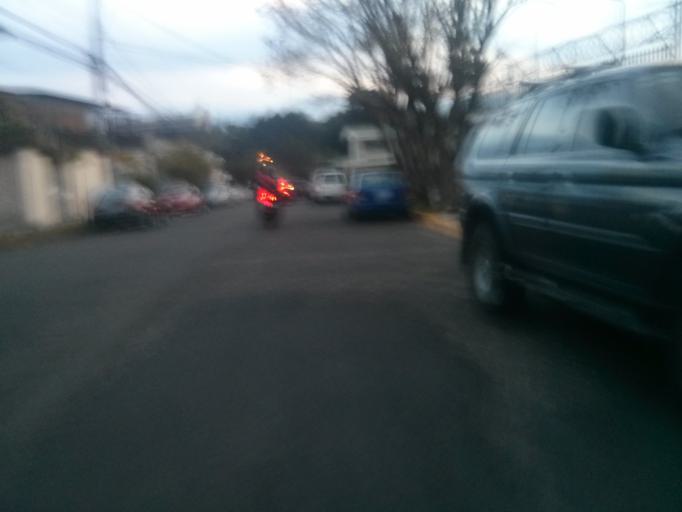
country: CR
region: San Jose
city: San Pedro
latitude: 9.9293
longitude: -84.0598
